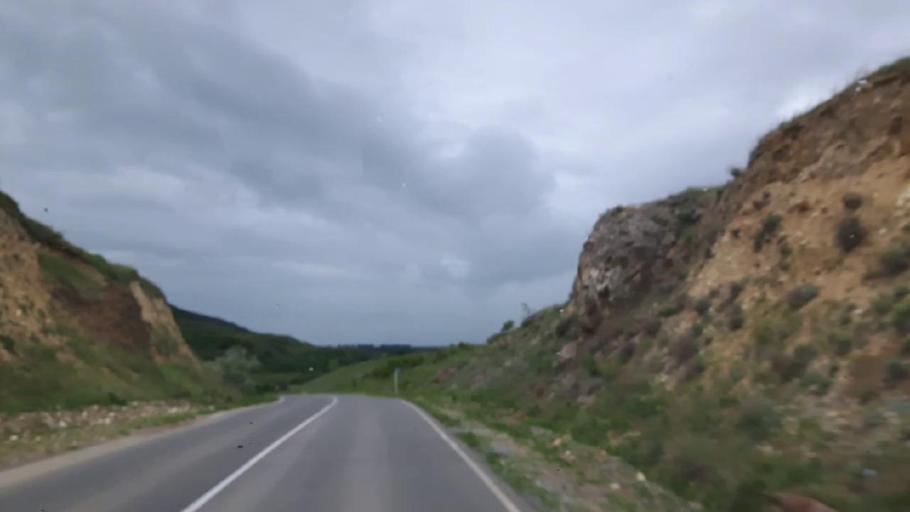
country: GE
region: Shida Kartli
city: Gori
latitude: 41.9910
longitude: 44.0379
